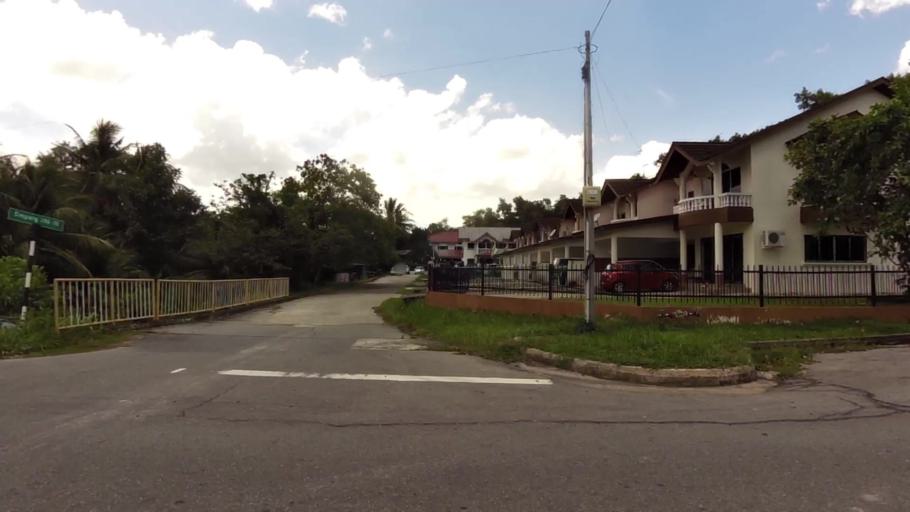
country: BN
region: Brunei and Muara
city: Bandar Seri Begawan
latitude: 4.9293
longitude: 114.9612
